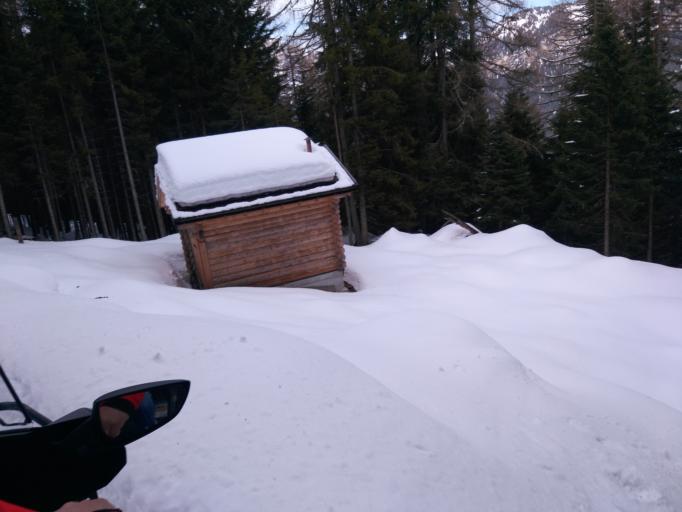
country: IT
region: Veneto
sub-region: Provincia di Belluno
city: Rocca Pietore
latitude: 46.4164
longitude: 11.9854
